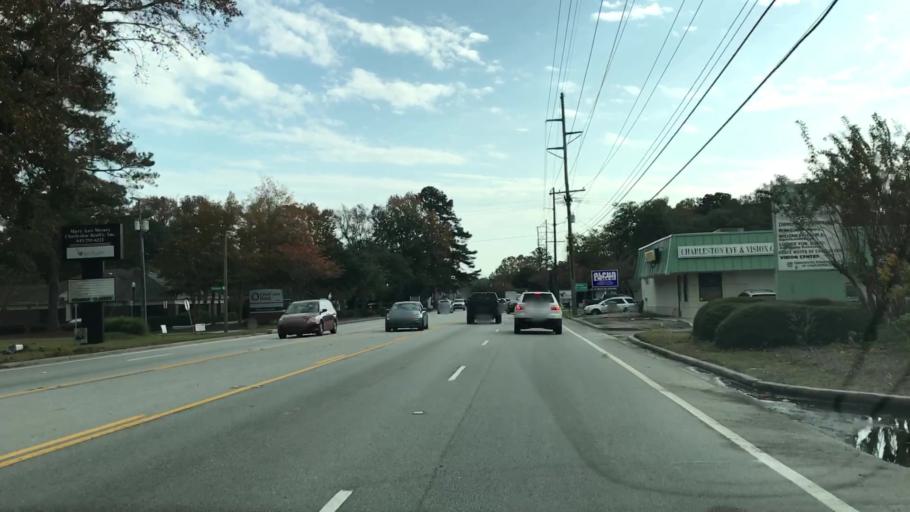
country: US
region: South Carolina
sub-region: Charleston County
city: Charleston
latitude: 32.7573
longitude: -79.9734
